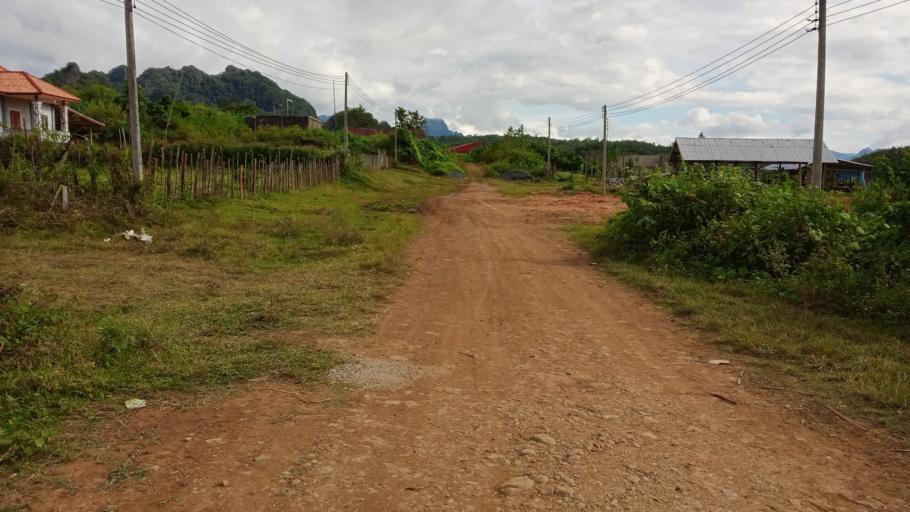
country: LA
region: Xiangkhoang
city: Phonsavan
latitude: 19.1059
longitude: 102.9283
